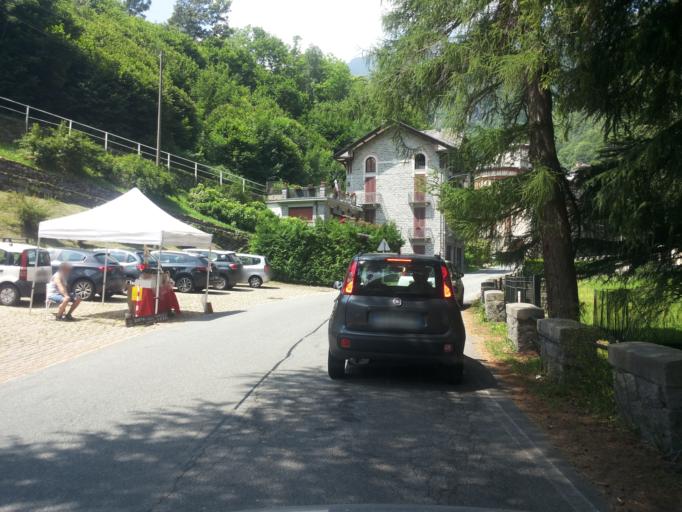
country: IT
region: Piedmont
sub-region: Provincia di Biella
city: Rosazza
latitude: 45.6750
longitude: 7.9804
